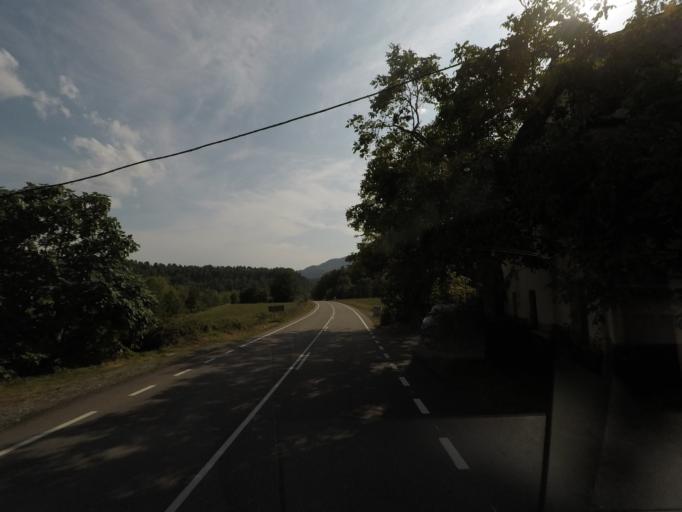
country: ES
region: Aragon
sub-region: Provincia de Huesca
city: Puertolas
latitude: 42.5270
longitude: 0.1456
